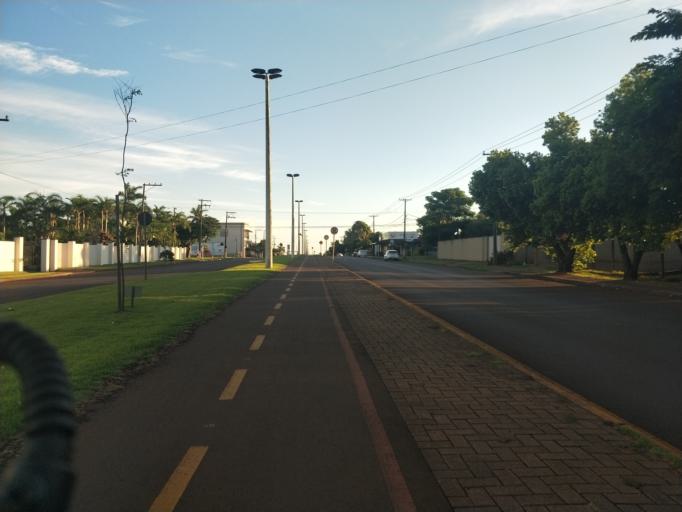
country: BR
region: Parana
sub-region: Marechal Candido Rondon
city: Marechal Candido Rondon
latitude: -24.5593
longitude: -54.0488
